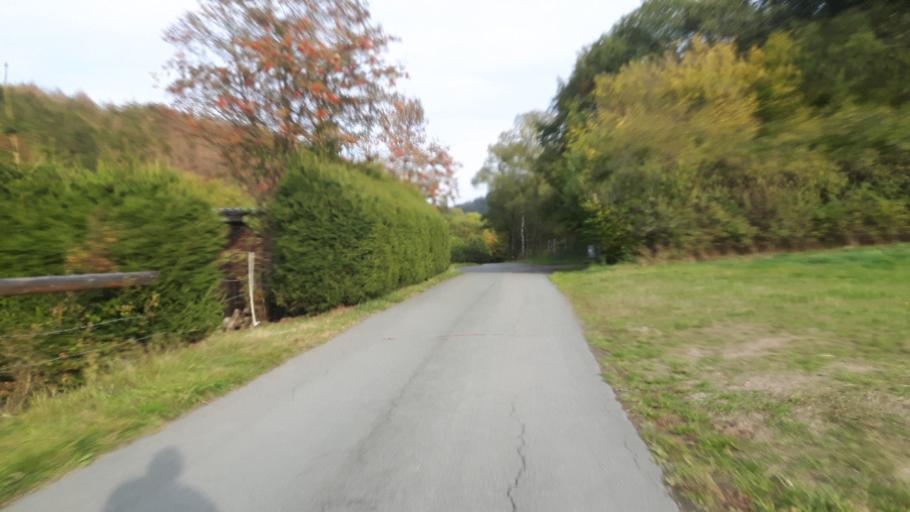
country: DE
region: North Rhine-Westphalia
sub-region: Regierungsbezirk Arnsberg
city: Bad Laasphe
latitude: 50.9196
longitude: 8.3927
